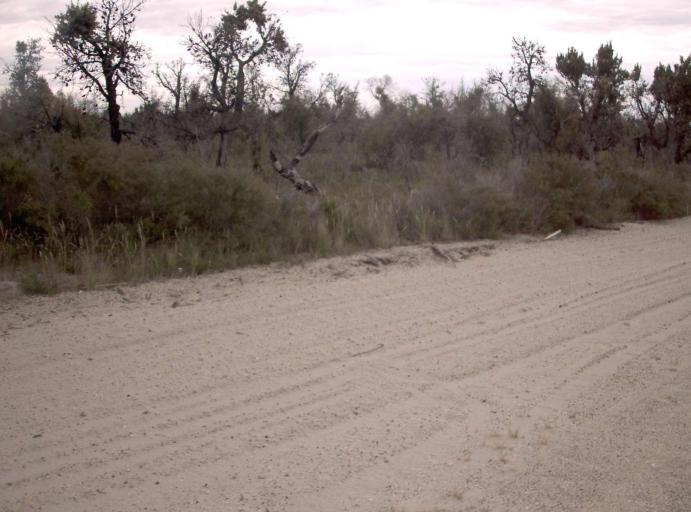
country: AU
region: Victoria
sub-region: East Gippsland
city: Bairnsdale
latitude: -38.1180
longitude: 147.4592
